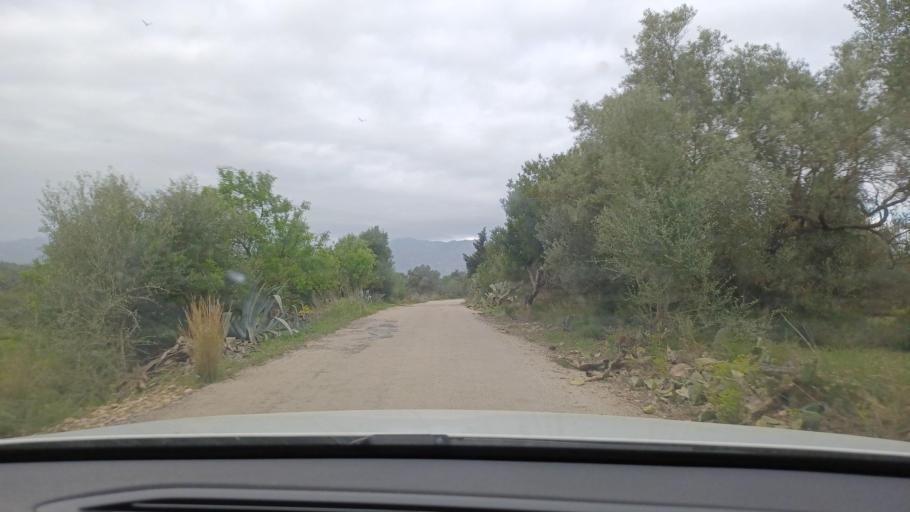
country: ES
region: Catalonia
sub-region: Provincia de Tarragona
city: Tortosa
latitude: 40.7904
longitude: 0.4802
